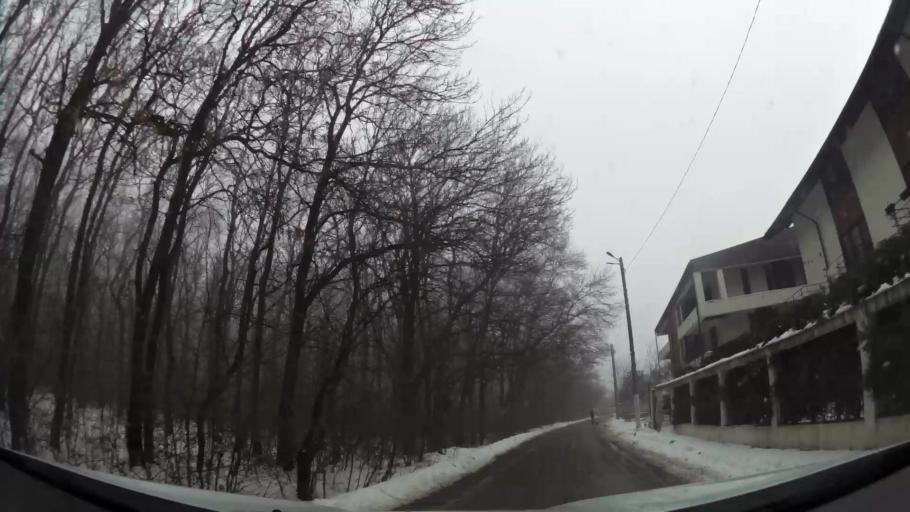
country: RO
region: Ilfov
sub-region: Comuna Chiajna
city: Rosu
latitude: 44.4553
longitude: 25.9983
